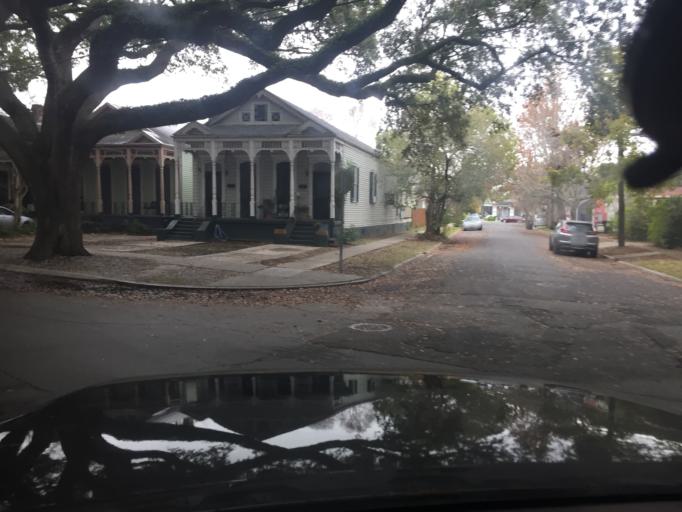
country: US
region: Louisiana
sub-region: Orleans Parish
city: New Orleans
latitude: 29.9763
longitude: -90.0835
